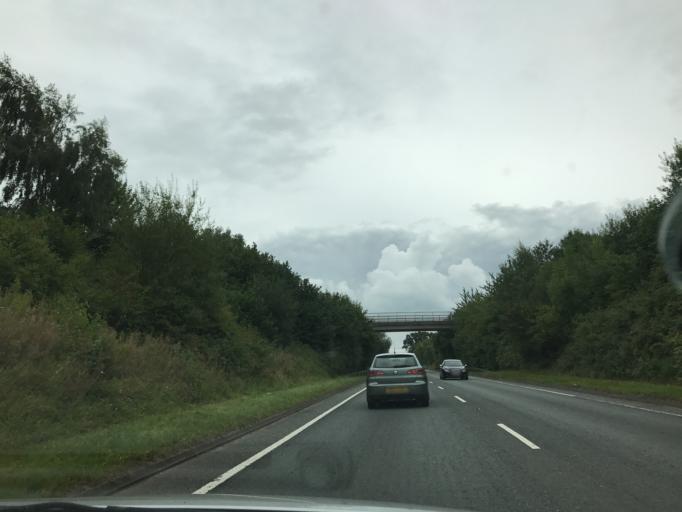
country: GB
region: England
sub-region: Cheshire West and Chester
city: Northwich
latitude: 53.2290
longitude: -2.5014
